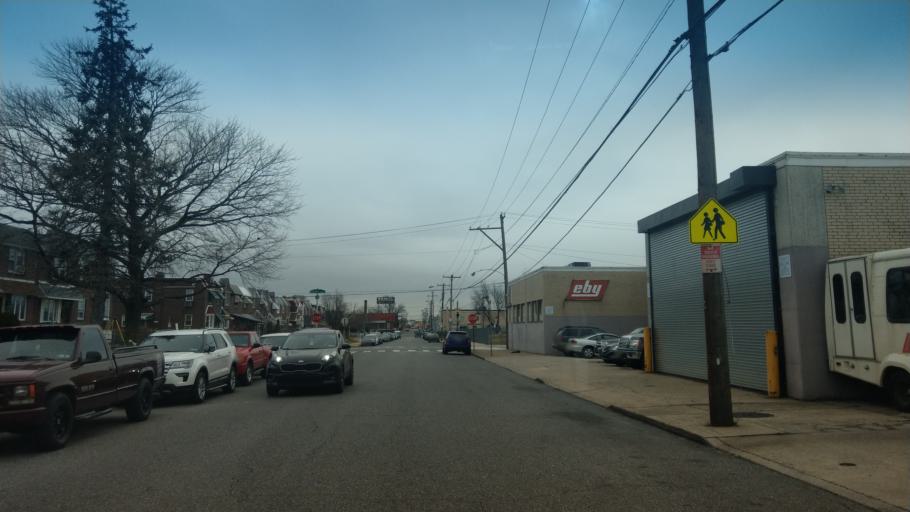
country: US
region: Pennsylvania
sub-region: Montgomery County
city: Rockledge
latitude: 40.0140
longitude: -75.1095
